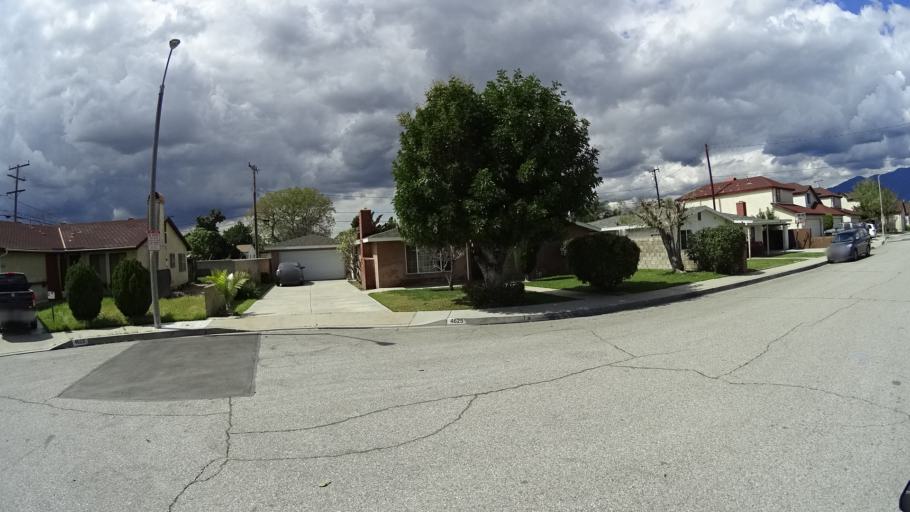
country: US
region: California
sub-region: Los Angeles County
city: Baldwin Park
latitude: 34.0962
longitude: -117.9624
